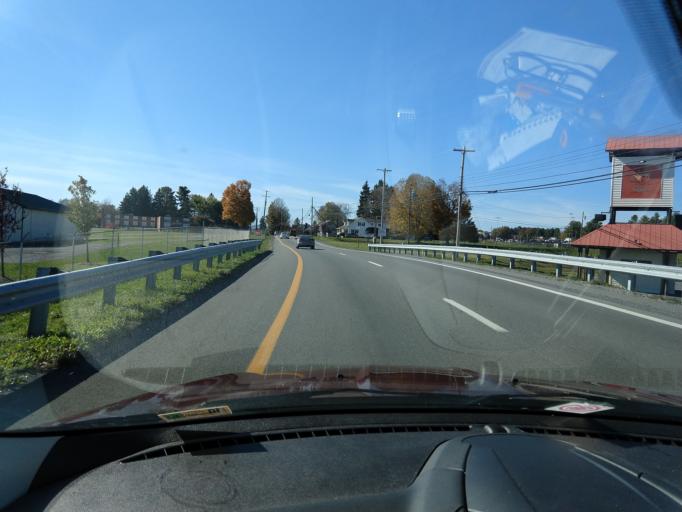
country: US
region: West Virginia
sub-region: Greenbrier County
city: Fairlea
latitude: 37.7779
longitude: -80.4641
